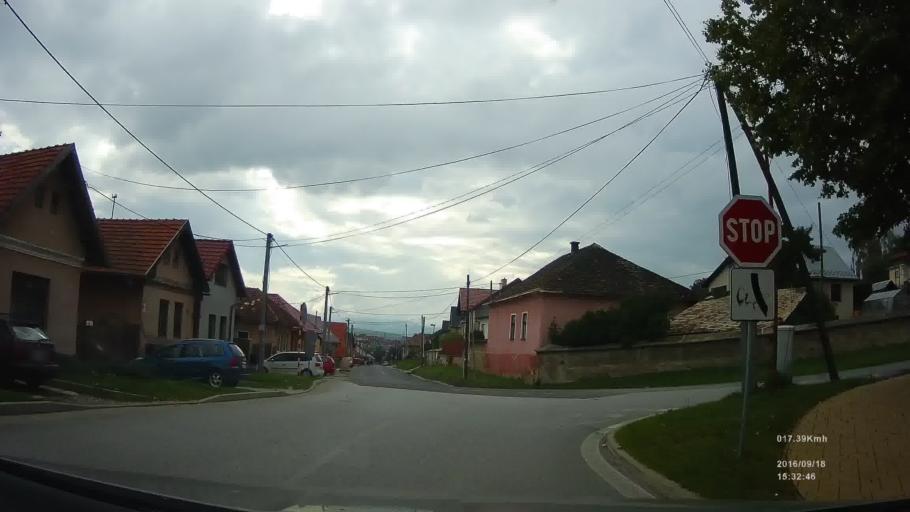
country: SK
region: Kosicky
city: Spisska Nova Ves
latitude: 49.0012
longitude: 20.4641
